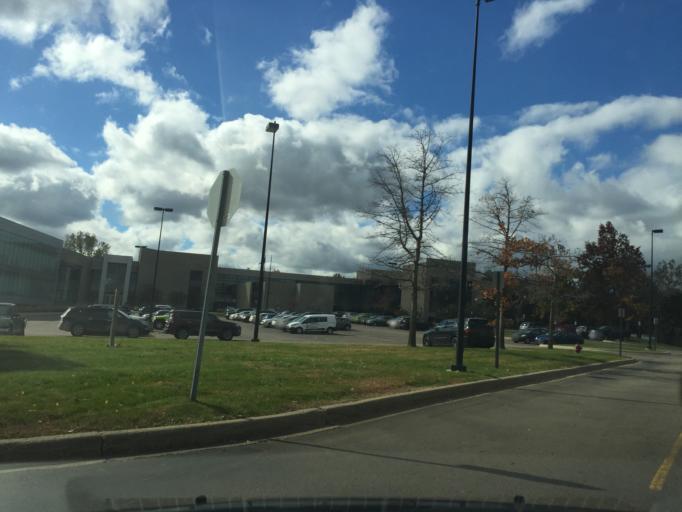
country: US
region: Michigan
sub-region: Oakland County
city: Auburn Hills
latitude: 42.6459
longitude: -83.2341
